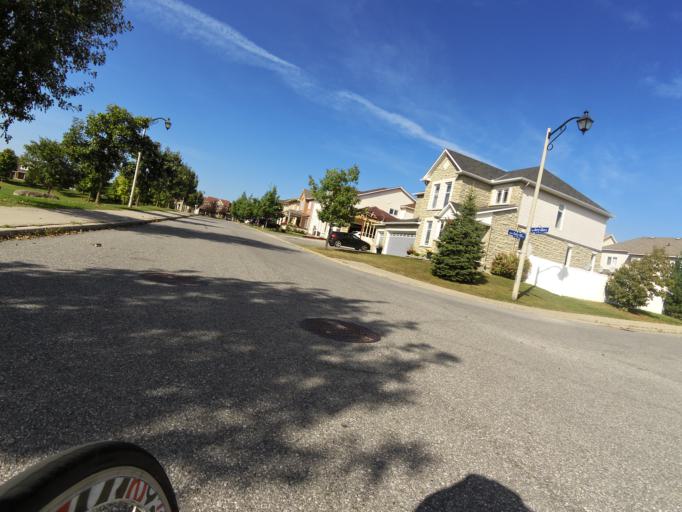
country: CA
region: Ontario
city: Bells Corners
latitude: 45.2673
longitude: -75.7120
